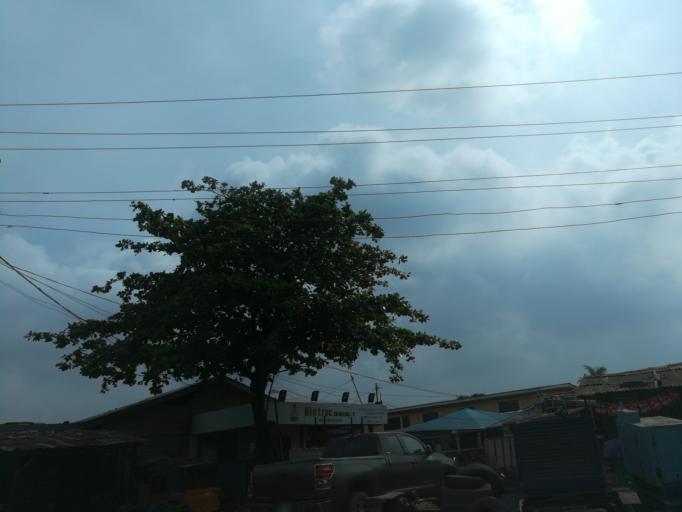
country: NG
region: Lagos
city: Agege
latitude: 6.5907
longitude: 3.3058
